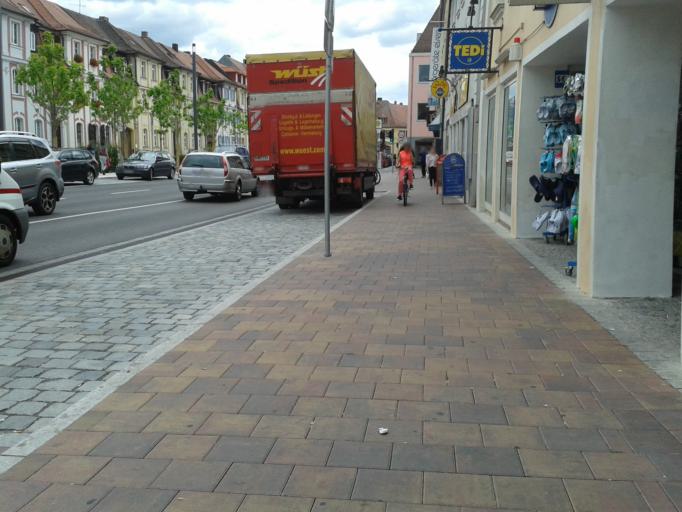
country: DE
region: Bavaria
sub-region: Regierungsbezirk Mittelfranken
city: Ansbach
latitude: 49.3005
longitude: 10.5714
